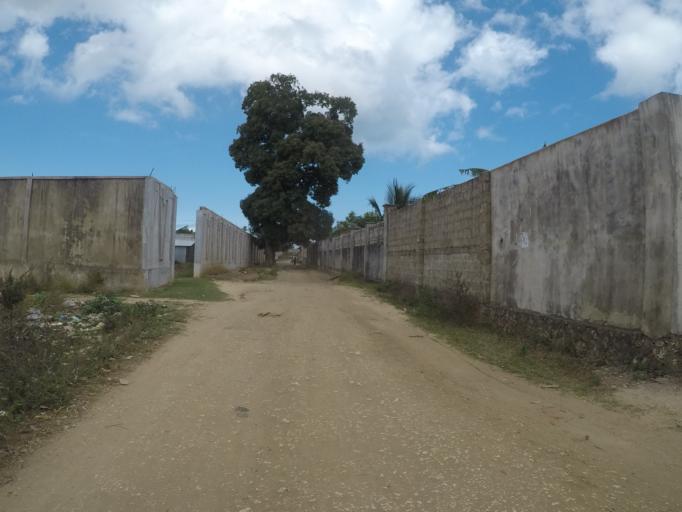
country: TZ
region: Zanzibar Urban/West
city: Zanzibar
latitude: -6.2055
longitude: 39.2291
